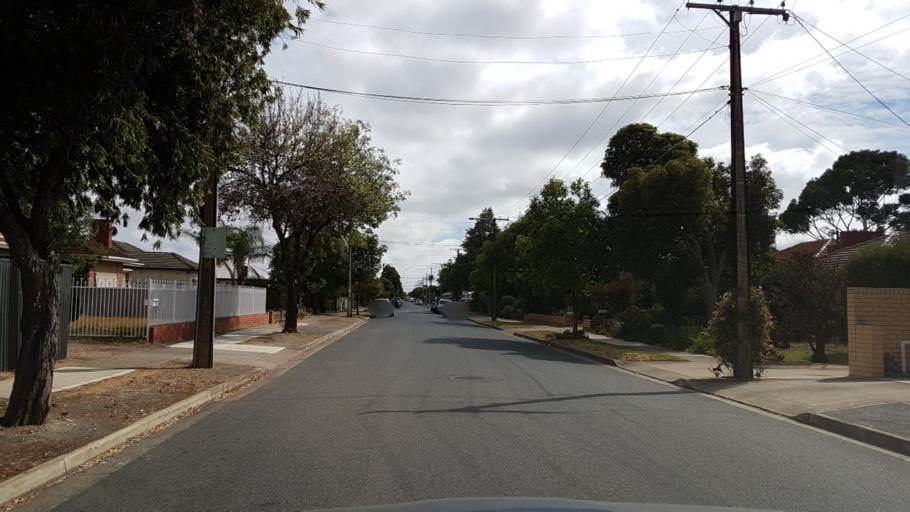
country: AU
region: South Australia
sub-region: Marion
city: Plympton Park
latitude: -34.9803
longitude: 138.5517
